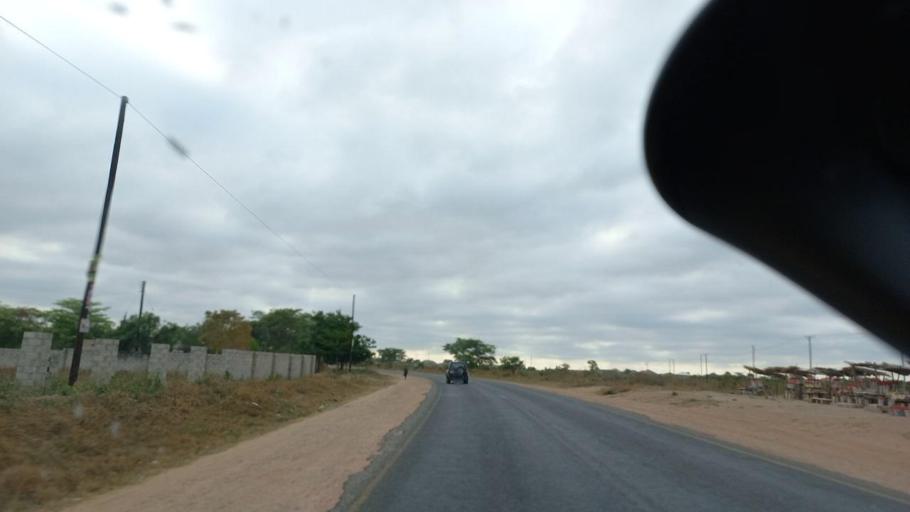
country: ZM
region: Lusaka
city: Chongwe
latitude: -15.3464
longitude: 28.6547
